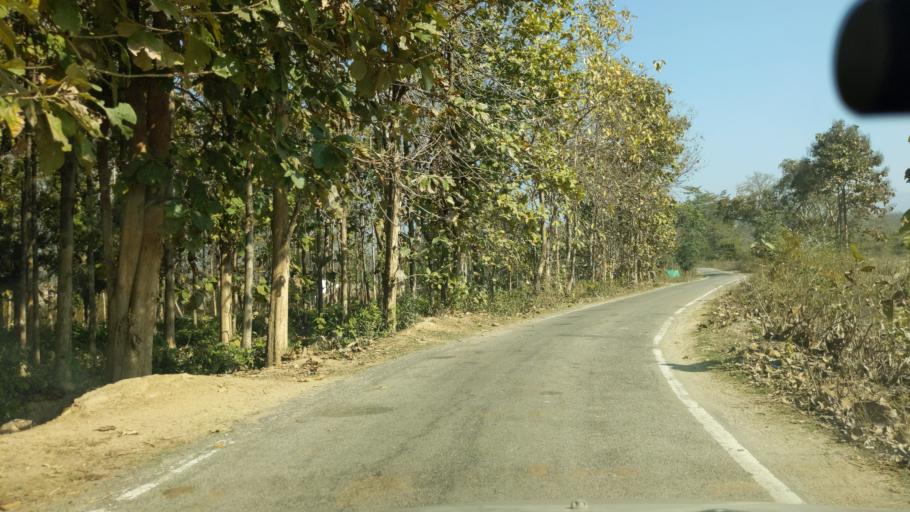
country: IN
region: Uttarakhand
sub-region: Naini Tal
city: Ramnagar
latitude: 29.4181
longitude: 79.1375
